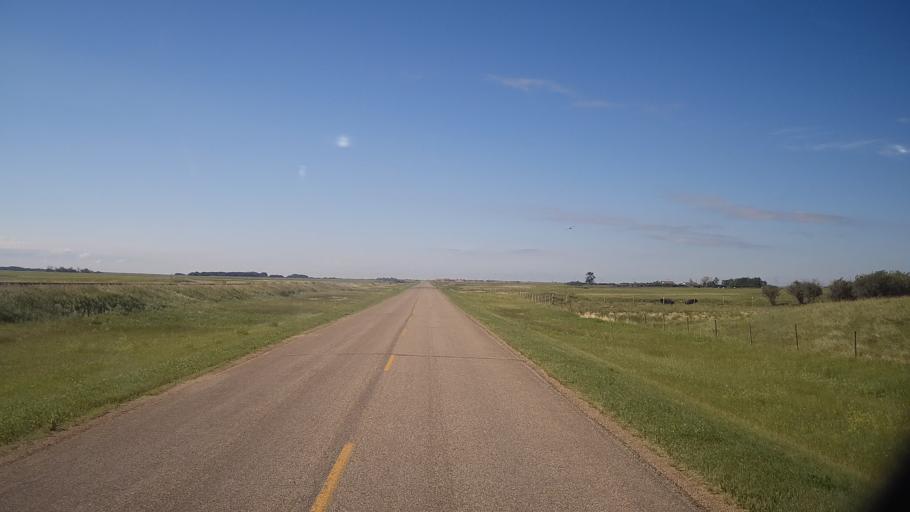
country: CA
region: Saskatchewan
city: Watrous
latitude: 51.7447
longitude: -105.2867
